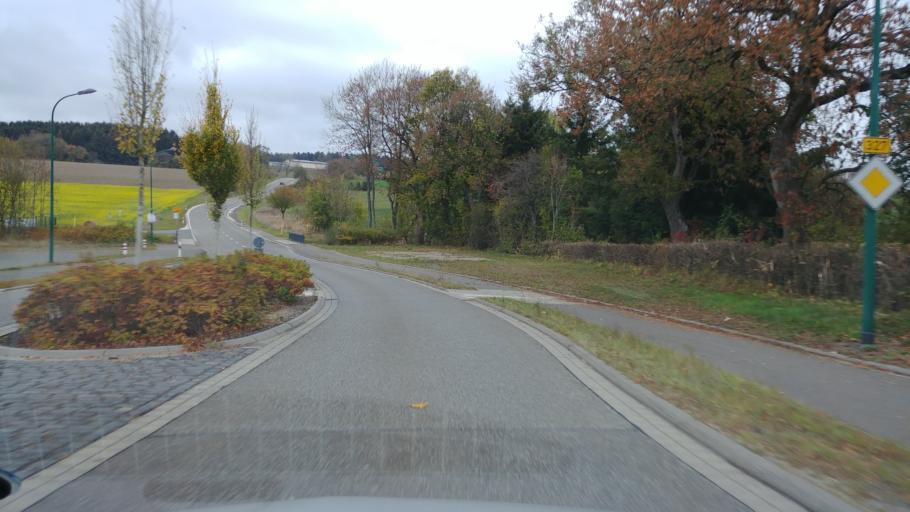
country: DE
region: Rheinland-Pfalz
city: Hermeskeil
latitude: 49.6636
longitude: 6.9492
